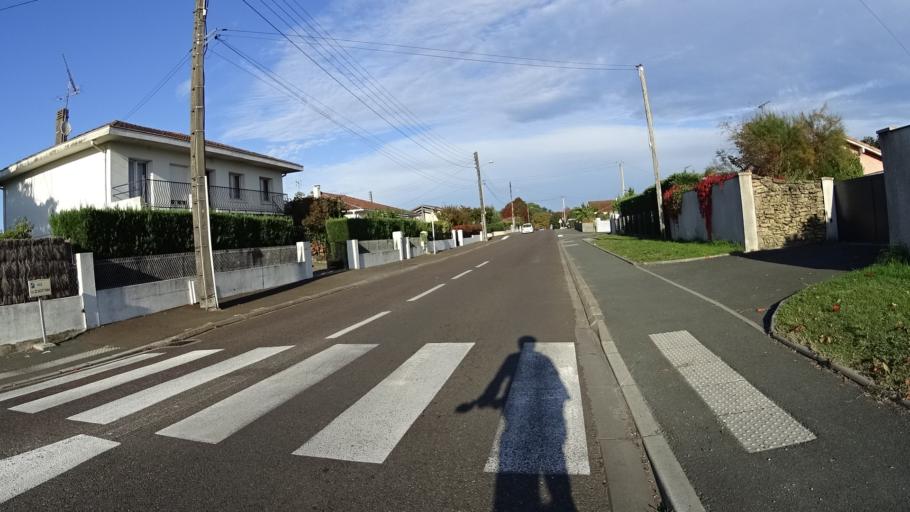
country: FR
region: Aquitaine
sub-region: Departement des Landes
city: Saint-Paul-les-Dax
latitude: 43.7354
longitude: -1.0540
